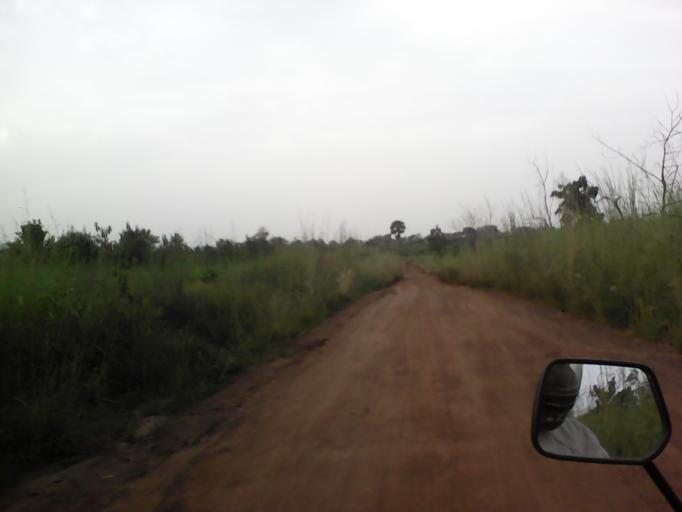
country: TG
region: Centrale
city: Sotouboua
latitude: 8.2257
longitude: 0.9772
